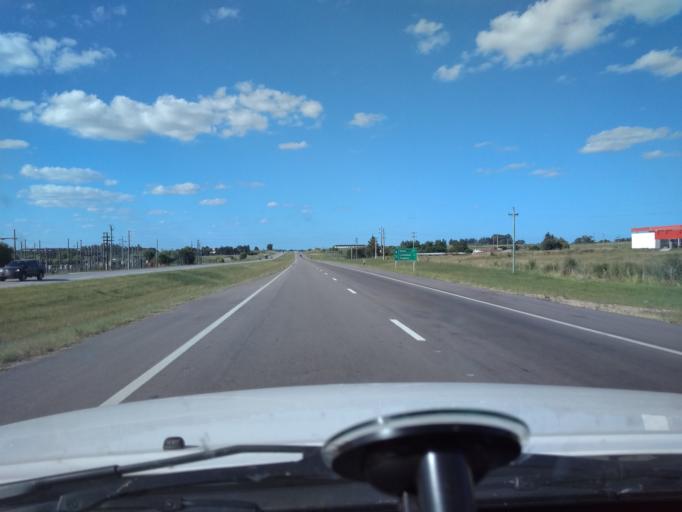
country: UY
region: Canelones
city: Las Piedras
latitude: -34.7146
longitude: -56.2437
